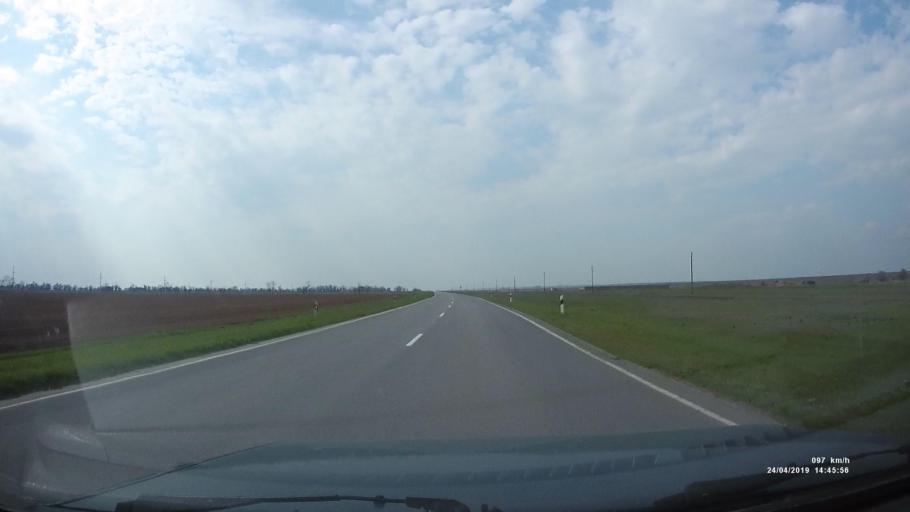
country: RU
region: Rostov
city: Remontnoye
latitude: 46.4772
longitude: 43.7986
